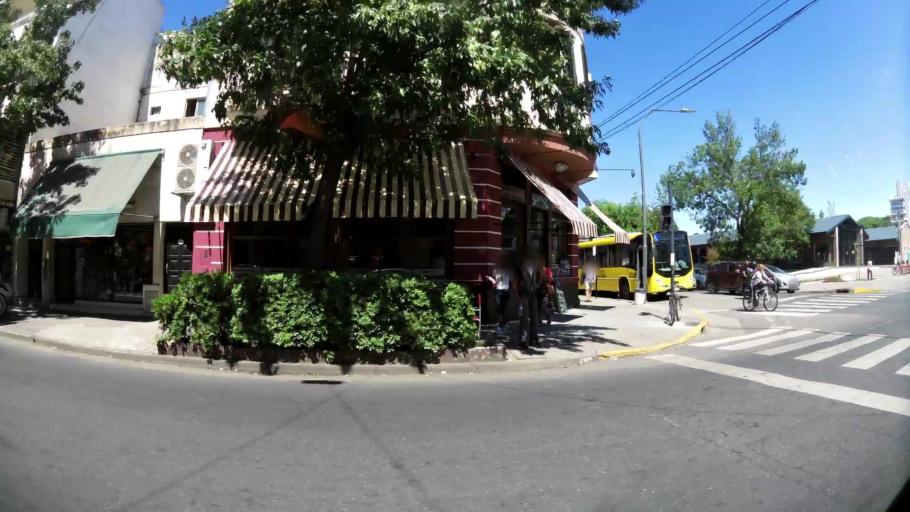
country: AR
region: Santa Fe
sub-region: Departamento de Rosario
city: Rosario
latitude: -32.9391
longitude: -60.6706
